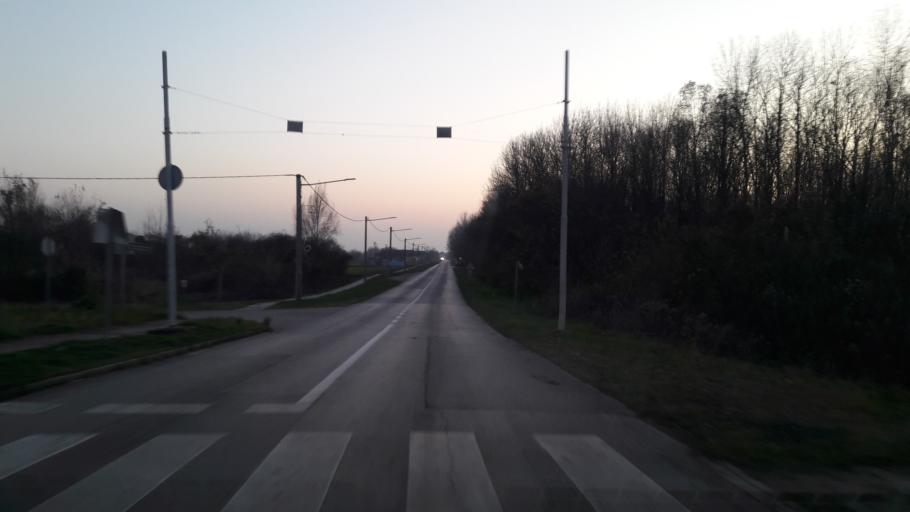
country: HR
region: Vukovarsko-Srijemska
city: Nijemci
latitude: 45.1937
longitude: 19.0197
